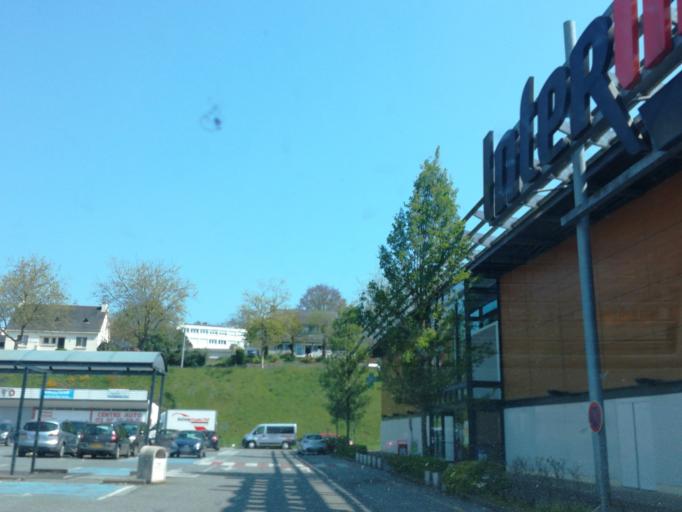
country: FR
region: Brittany
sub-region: Departement du Morbihan
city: Pontivy
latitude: 48.0528
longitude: -2.9581
